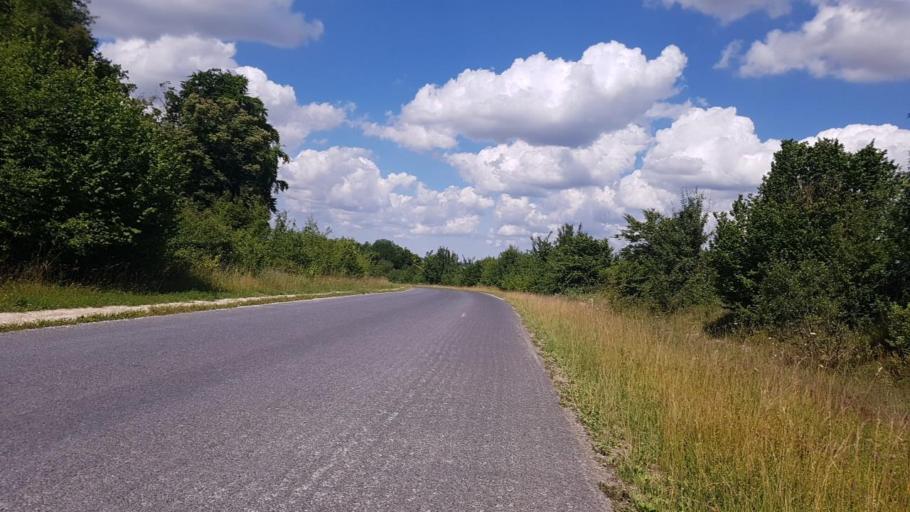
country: FR
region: Lorraine
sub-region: Departement de la Meuse
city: Vacon
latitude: 48.6884
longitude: 5.6704
